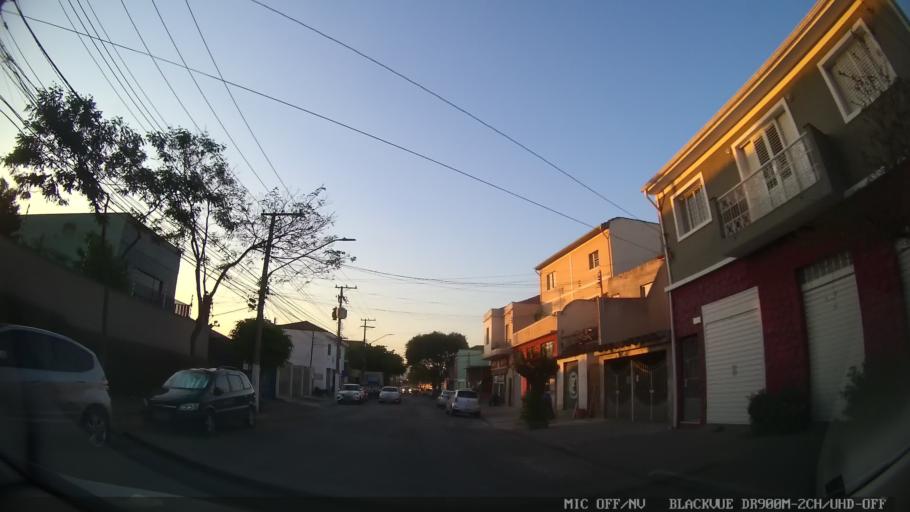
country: BR
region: Sao Paulo
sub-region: Sao Paulo
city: Sao Paulo
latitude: -23.4969
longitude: -46.6438
